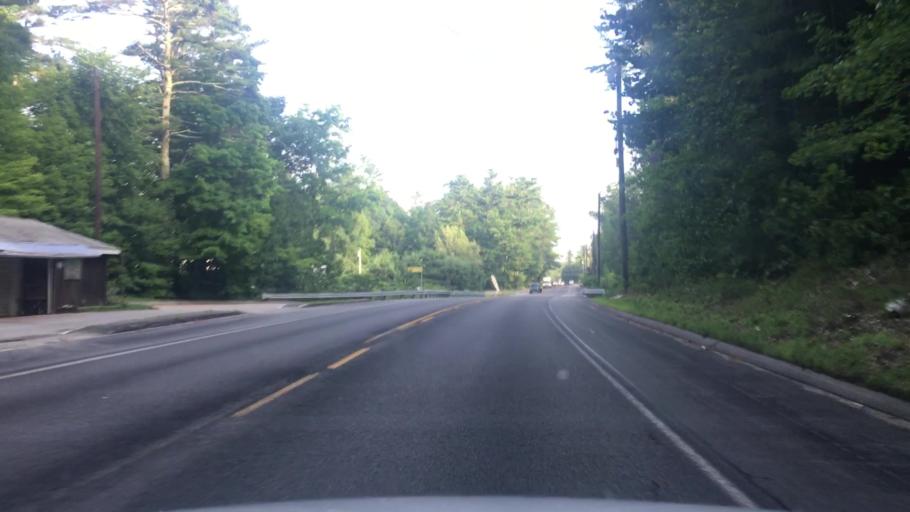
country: US
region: Maine
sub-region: Cumberland County
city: North Windham
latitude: 43.7937
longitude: -70.3987
